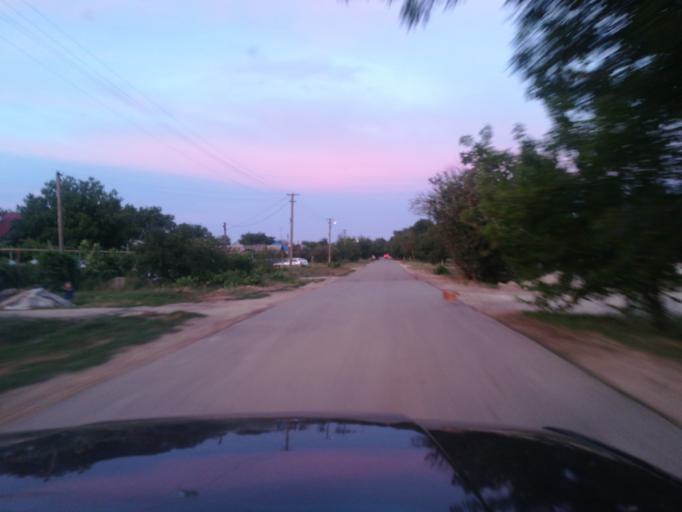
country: RU
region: Krasnodarskiy
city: Yurovka
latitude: 45.1142
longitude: 37.4297
